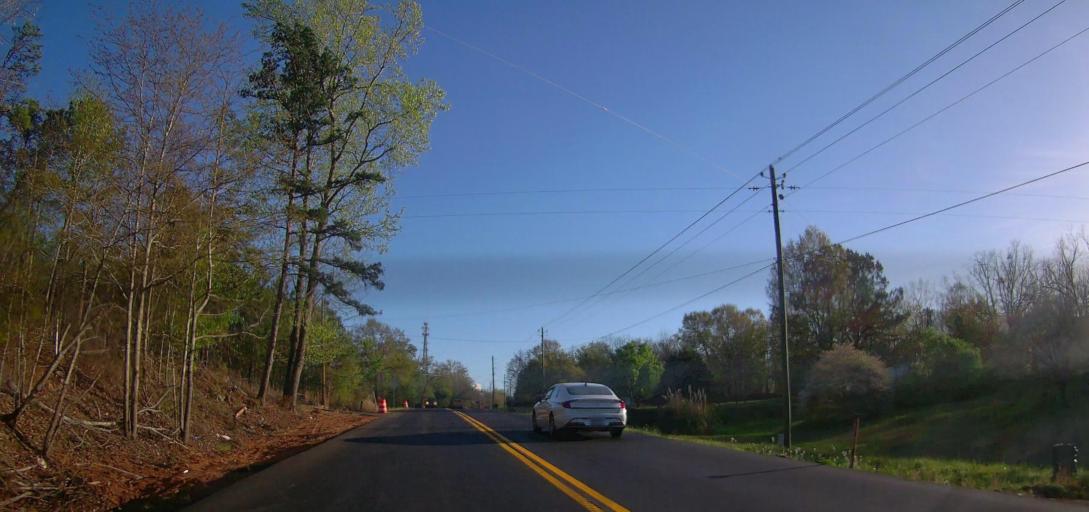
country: US
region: Georgia
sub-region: Newton County
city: Porterdale
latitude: 33.5511
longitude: -83.9116
